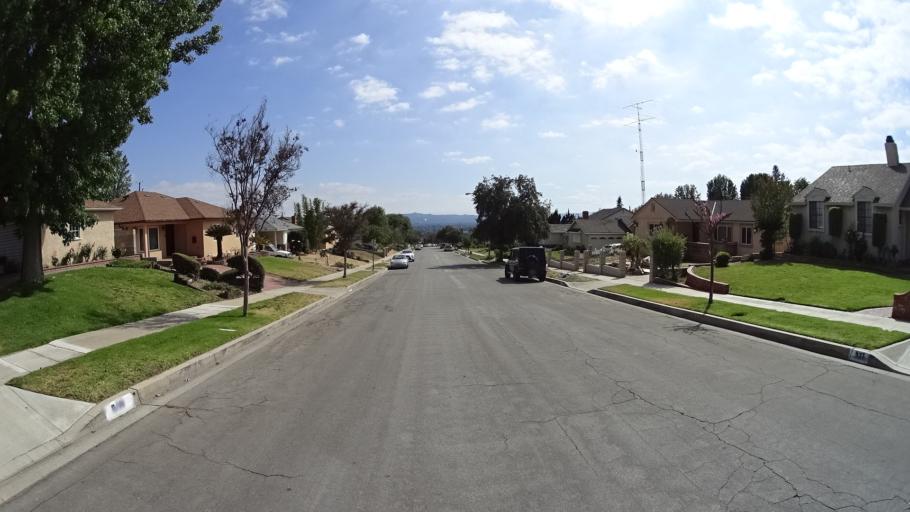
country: US
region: California
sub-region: Los Angeles County
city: Burbank
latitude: 34.1992
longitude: -118.3120
